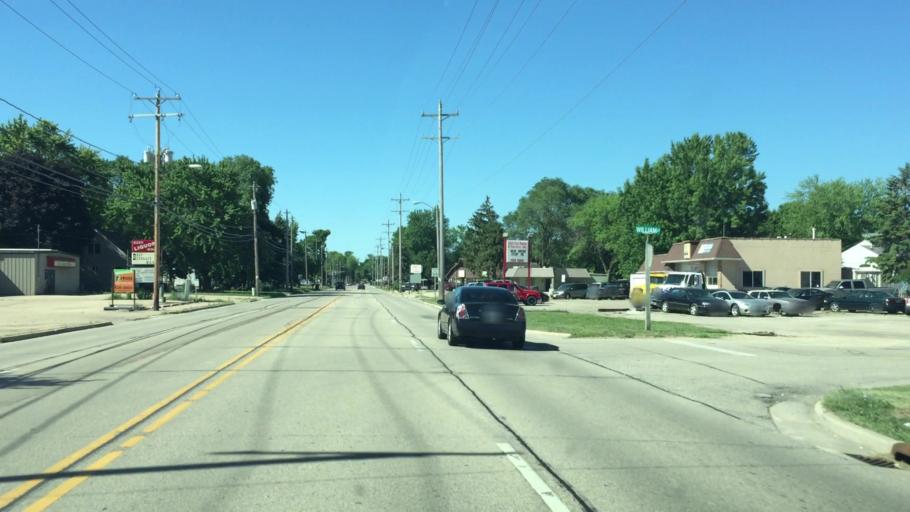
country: US
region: Wisconsin
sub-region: Winnebago County
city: Menasha
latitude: 44.2189
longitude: -88.4304
